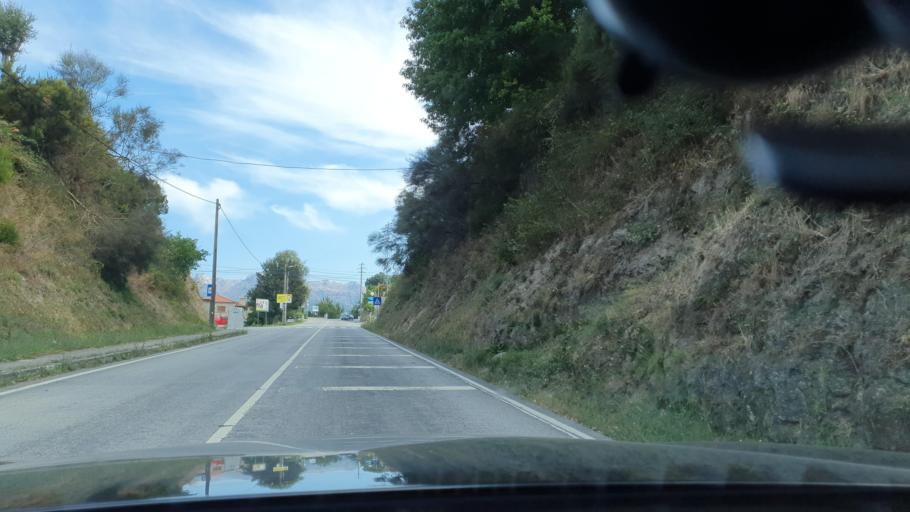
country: PT
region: Braga
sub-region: Vieira do Minho
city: Vieira do Minho
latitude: 41.6780
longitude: -8.1179
